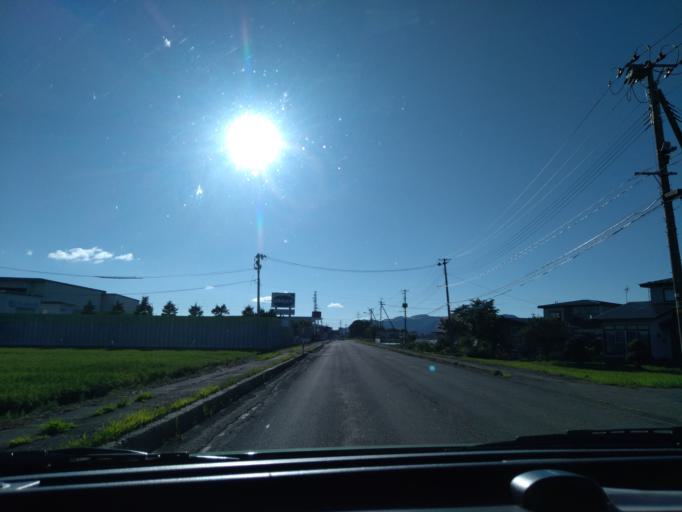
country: JP
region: Akita
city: Omagari
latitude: 39.4243
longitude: 140.5003
